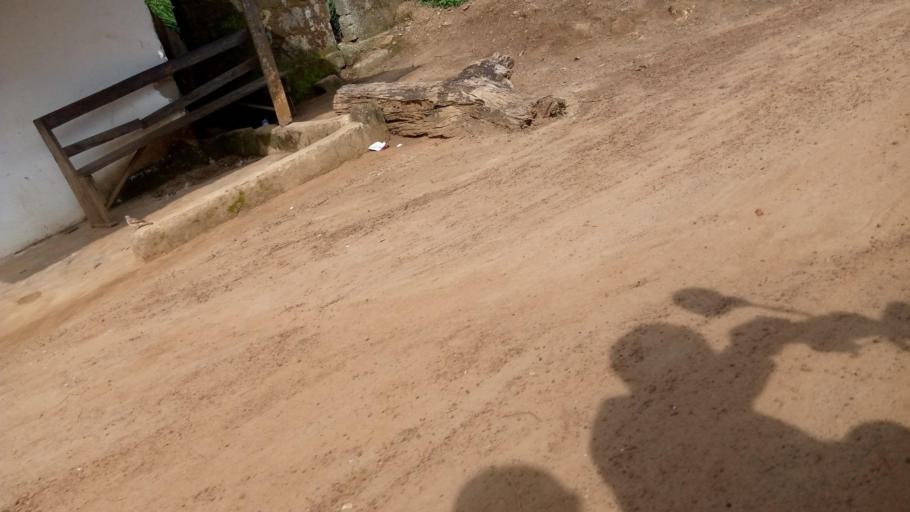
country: SL
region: Southern Province
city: Pujehun
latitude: 7.3546
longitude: -11.7190
